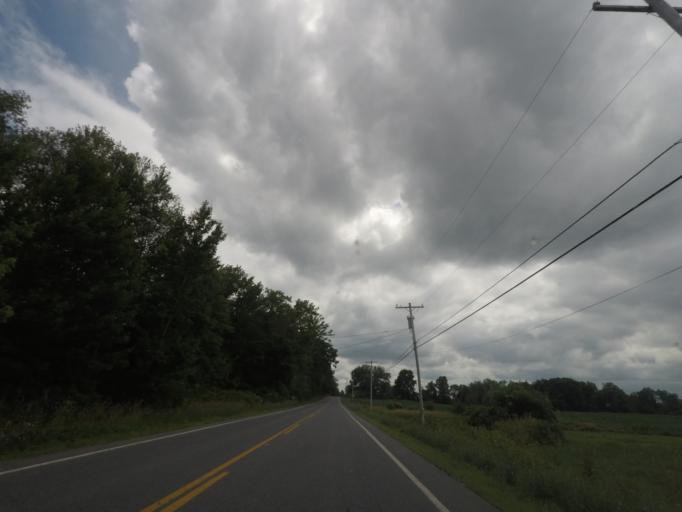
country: US
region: New York
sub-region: Saratoga County
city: Stillwater
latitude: 43.0219
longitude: -73.6905
